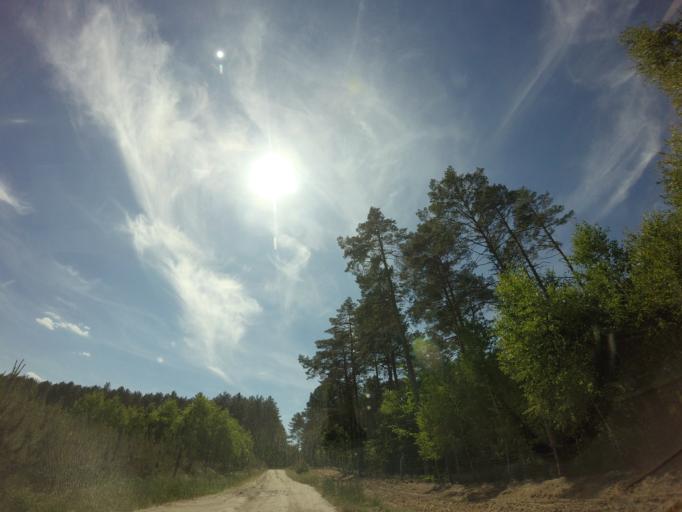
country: PL
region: West Pomeranian Voivodeship
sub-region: Powiat choszczenski
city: Drawno
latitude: 53.1270
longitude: 15.8328
